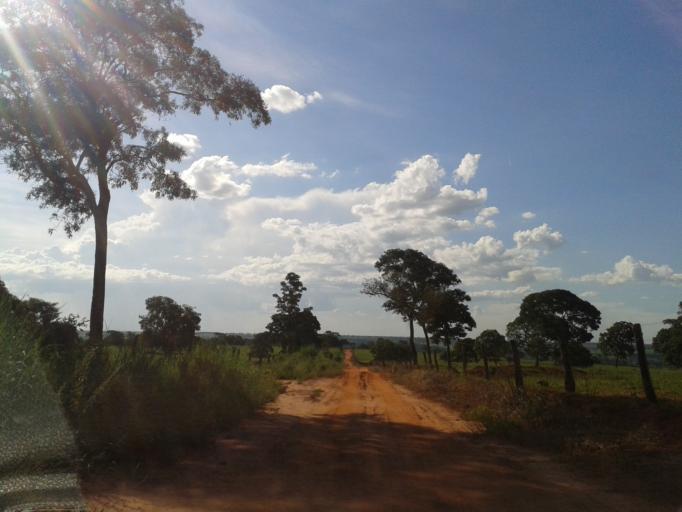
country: BR
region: Minas Gerais
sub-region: Santa Vitoria
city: Santa Vitoria
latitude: -19.1094
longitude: -50.5072
